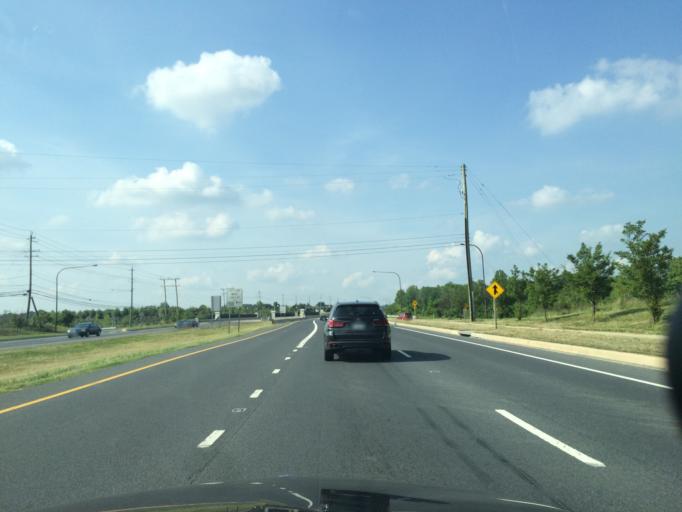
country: US
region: Maryland
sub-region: Montgomery County
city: Rossmoor
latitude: 39.1161
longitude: -77.0750
